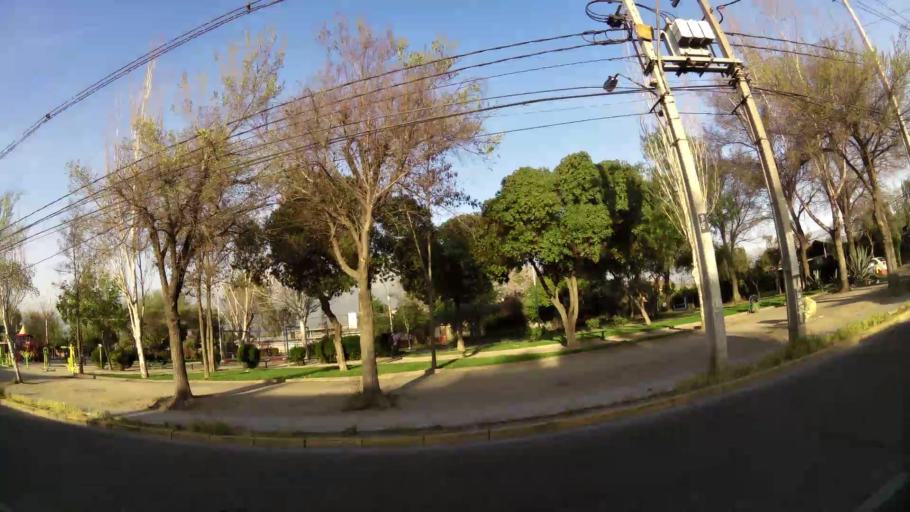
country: CL
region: Santiago Metropolitan
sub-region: Provincia de Santiago
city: La Pintana
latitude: -33.5490
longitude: -70.5829
